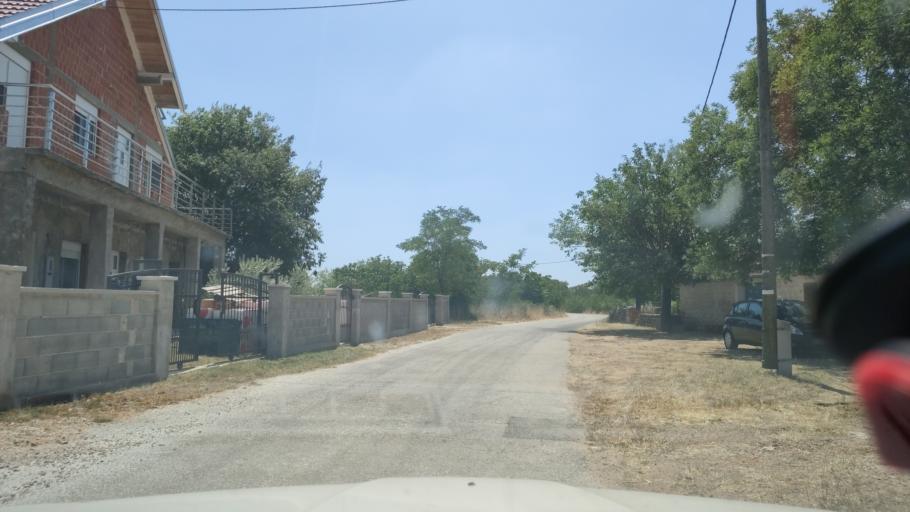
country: HR
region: Sibensko-Kniniska
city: Kistanje
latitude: 43.9523
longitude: 15.8818
